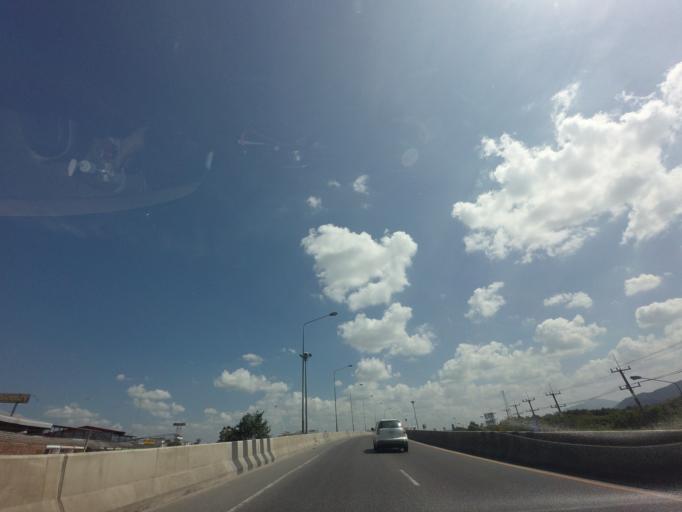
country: TH
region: Chon Buri
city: Ban Bueng
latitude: 13.3174
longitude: 101.1034
